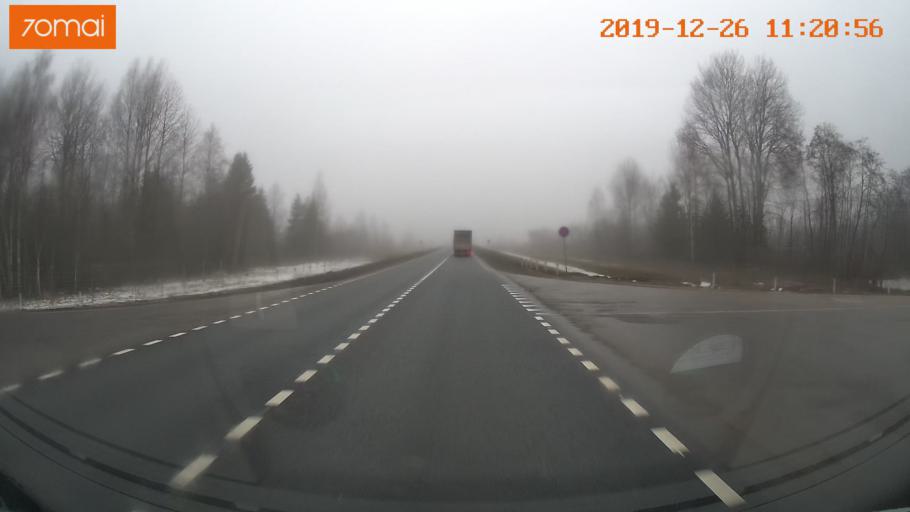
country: RU
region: Vologda
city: Chebsara
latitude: 59.1215
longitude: 38.9773
